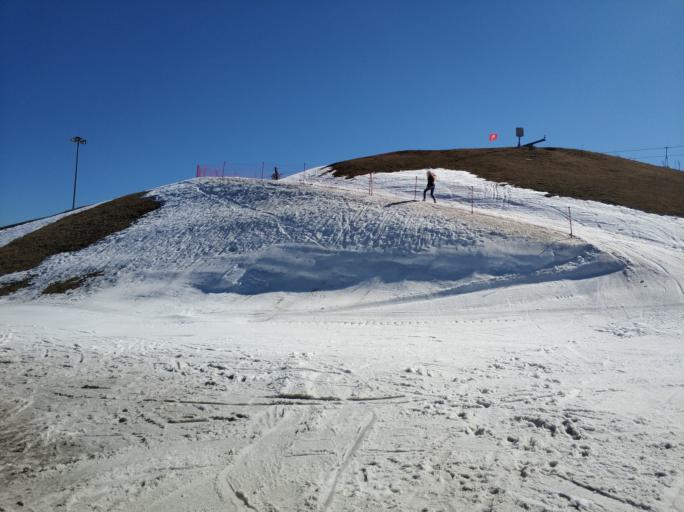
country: RU
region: Leningrad
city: Sosnovo
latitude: 60.5151
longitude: 30.2116
